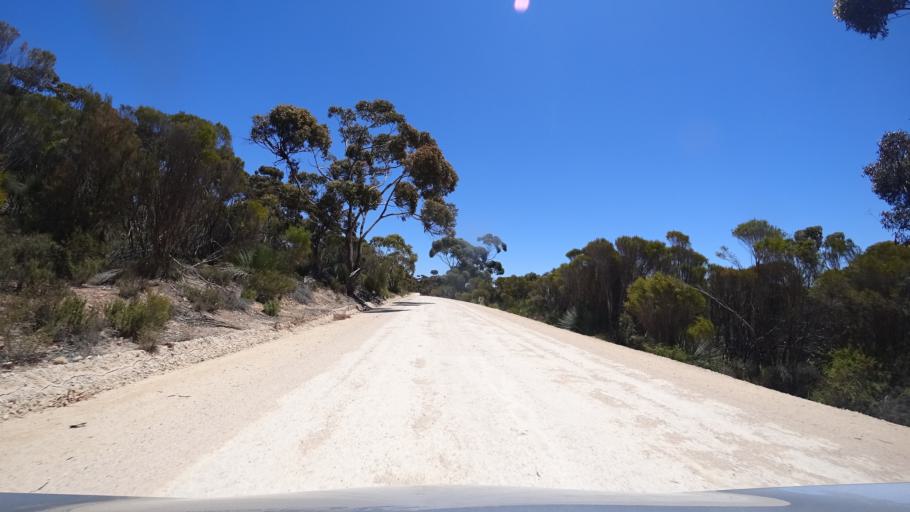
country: AU
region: South Australia
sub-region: Kangaroo Island
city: Kingscote
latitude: -35.6510
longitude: 137.1712
